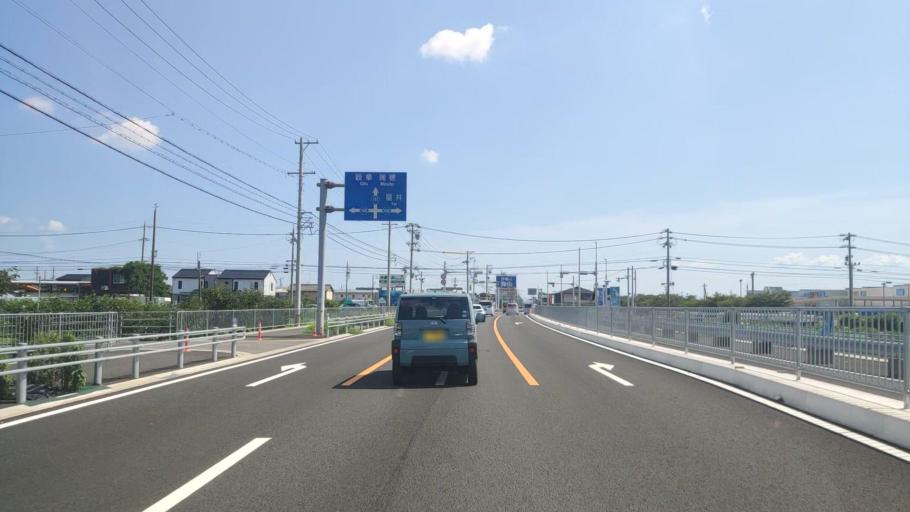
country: JP
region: Gifu
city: Godo
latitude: 35.4595
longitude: 136.6762
